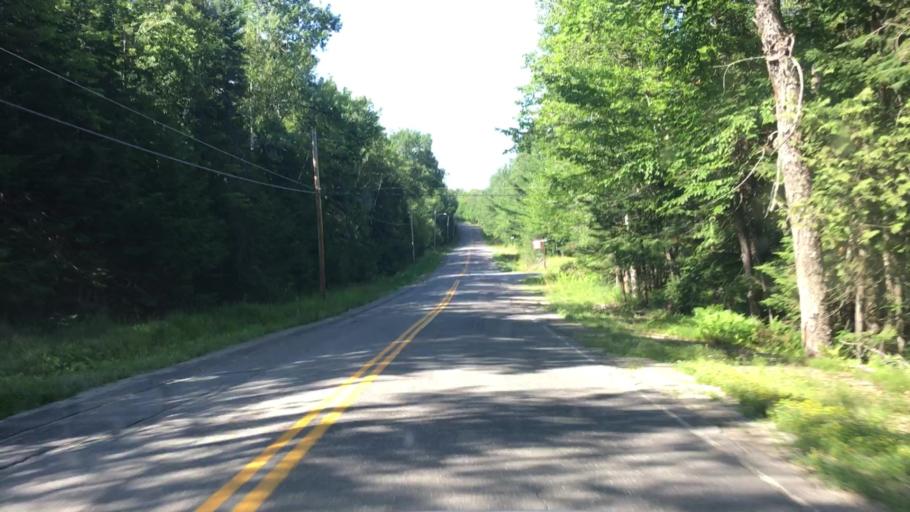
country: US
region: Maine
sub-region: Penobscot County
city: Enfield
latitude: 45.2711
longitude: -68.5610
